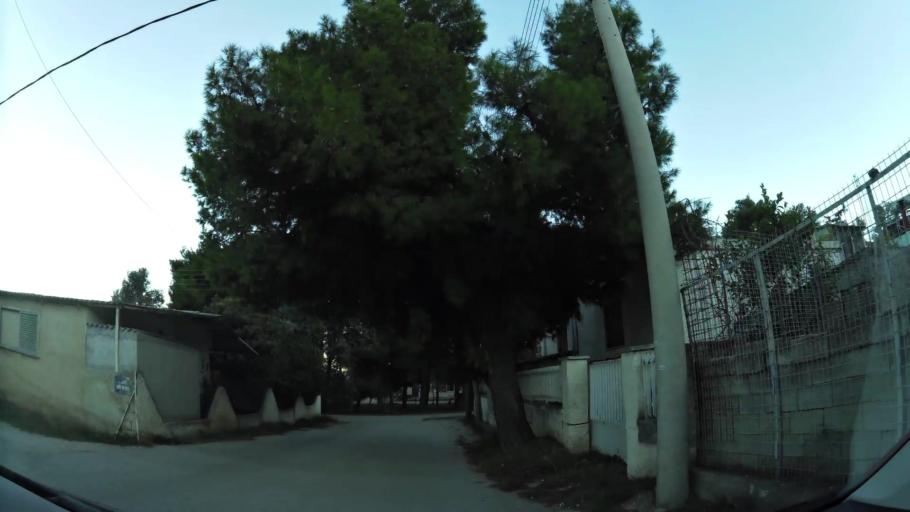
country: GR
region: Attica
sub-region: Nomarchia Anatolikis Attikis
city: Leondarion
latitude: 37.9716
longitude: 23.8493
